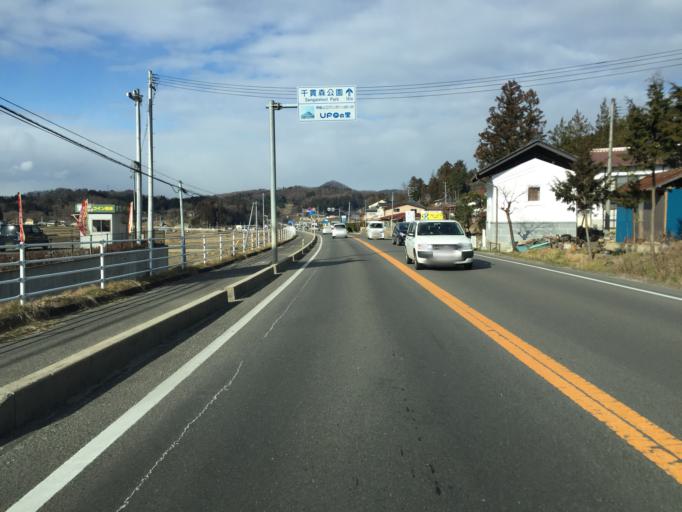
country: JP
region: Fukushima
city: Fukushima-shi
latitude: 37.6693
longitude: 140.5736
